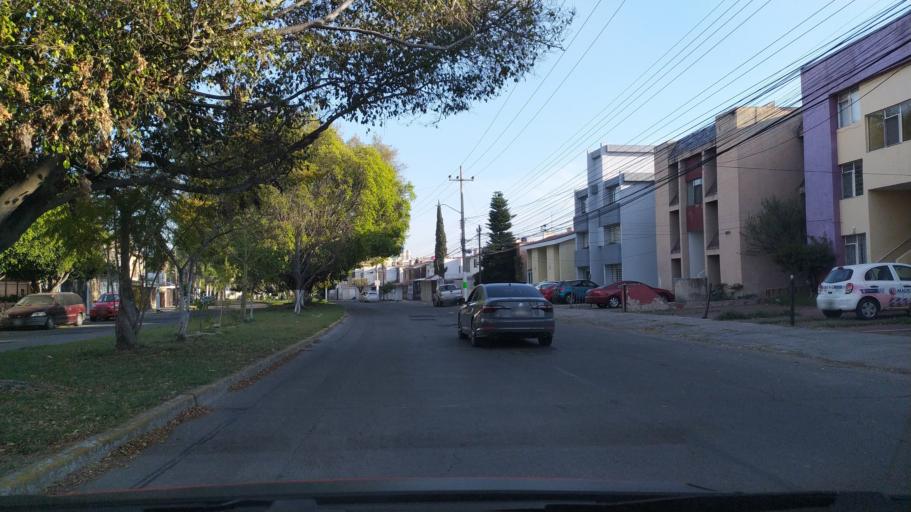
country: MX
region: Jalisco
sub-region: Tlajomulco de Zuniga
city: Palomar
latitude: 20.6288
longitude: -103.4282
